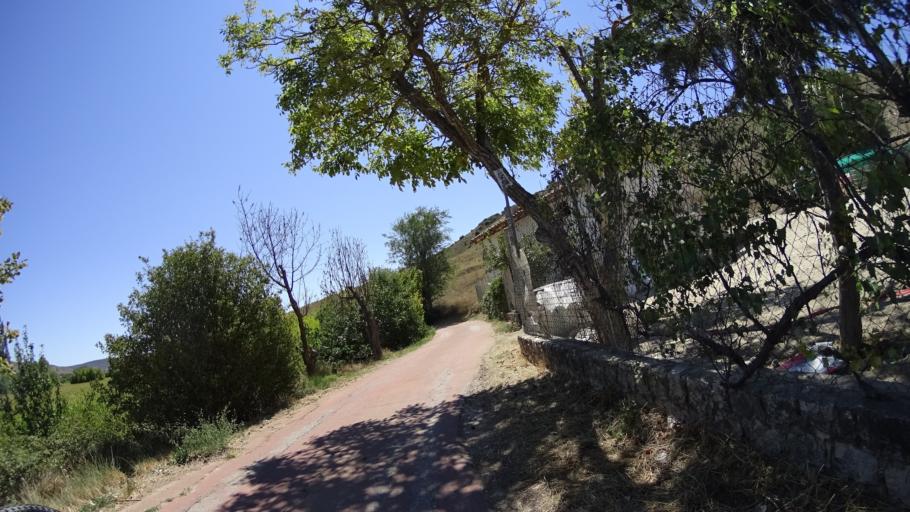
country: ES
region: Madrid
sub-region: Provincia de Madrid
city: Tielmes
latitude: 40.2425
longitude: -3.2751
